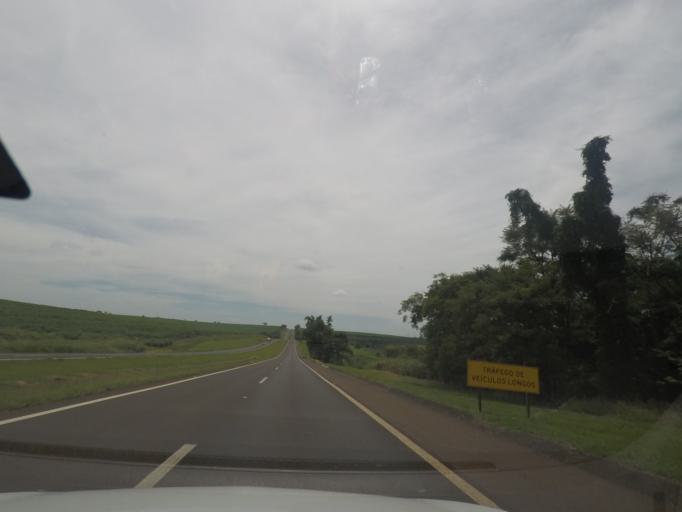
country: BR
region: Sao Paulo
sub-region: Bebedouro
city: Bebedouro
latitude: -21.0374
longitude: -48.4185
